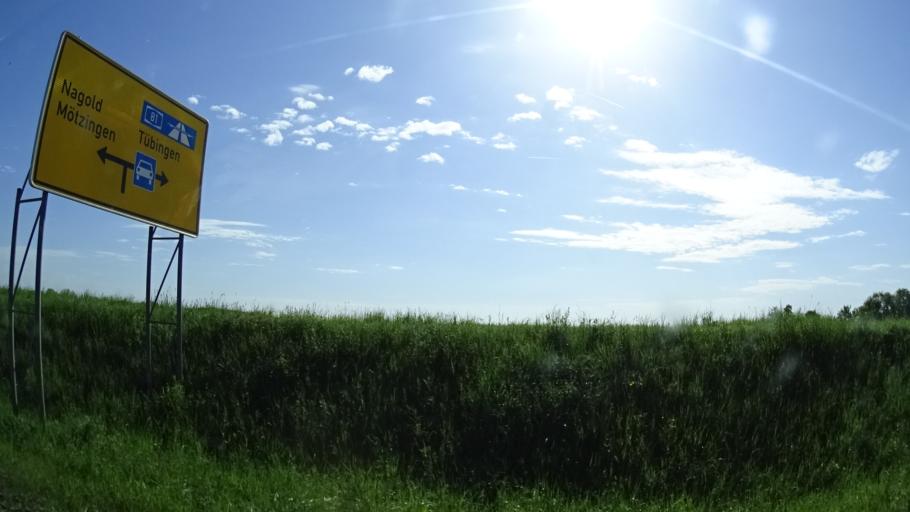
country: DE
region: Baden-Wuerttemberg
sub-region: Regierungsbezirk Stuttgart
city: Motzingen
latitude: 48.5092
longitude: 8.7782
